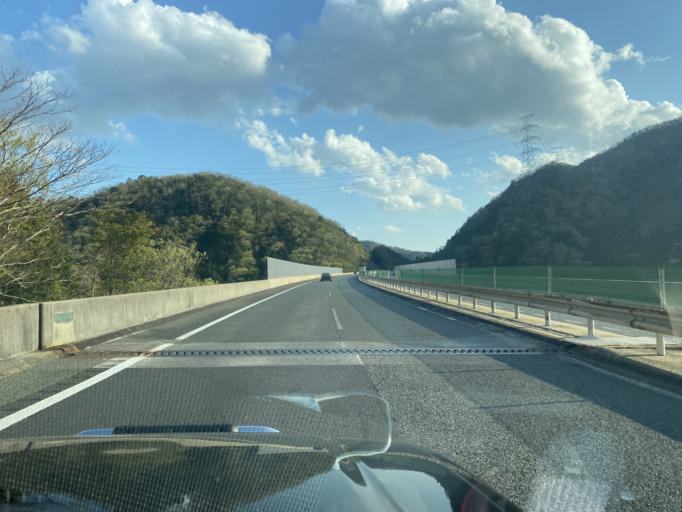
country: JP
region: Hyogo
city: Sasayama
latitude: 34.9931
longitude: 135.1562
